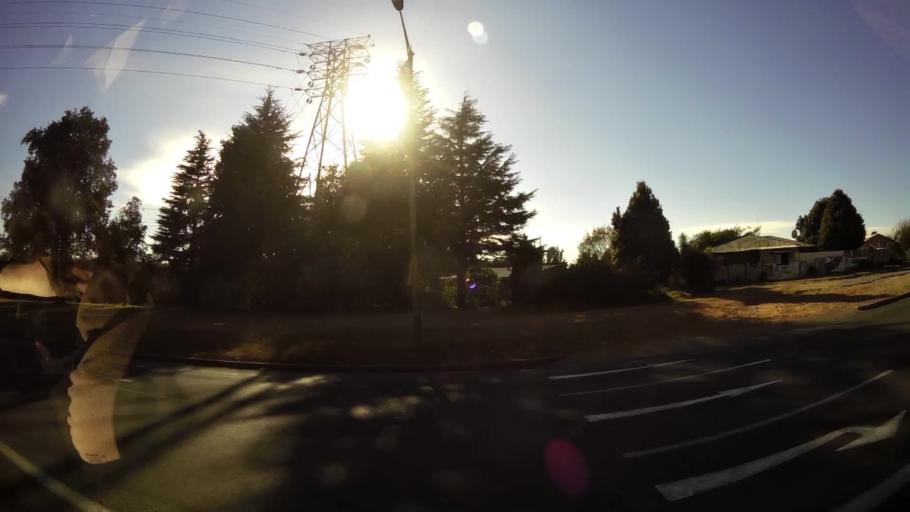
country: ZA
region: Gauteng
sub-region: West Rand District Municipality
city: Krugersdorp
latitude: -26.1186
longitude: 27.8018
